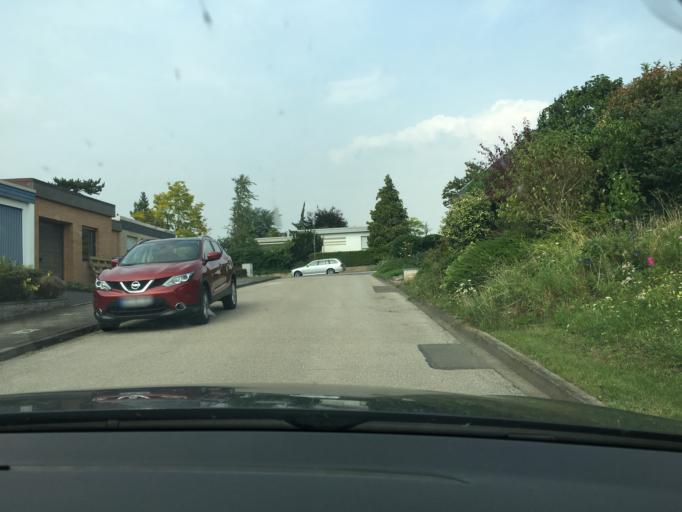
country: DE
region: North Rhine-Westphalia
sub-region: Regierungsbezirk Koln
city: Dueren
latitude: 50.7904
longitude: 6.4971
